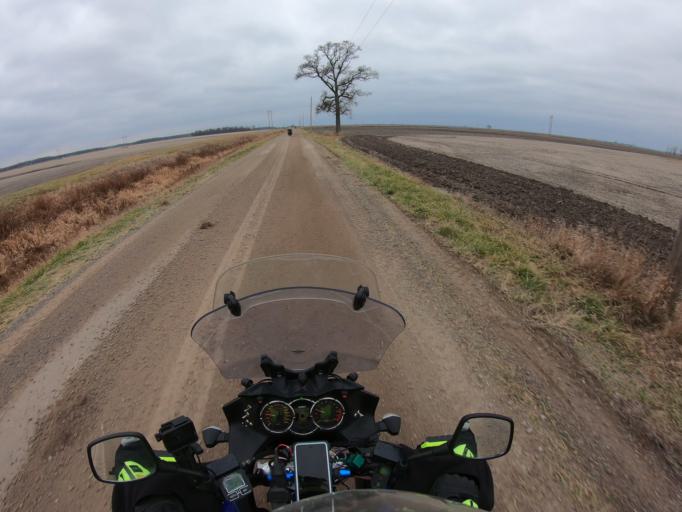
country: US
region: Michigan
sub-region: Saginaw County
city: Burt
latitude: 43.2648
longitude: -83.9768
